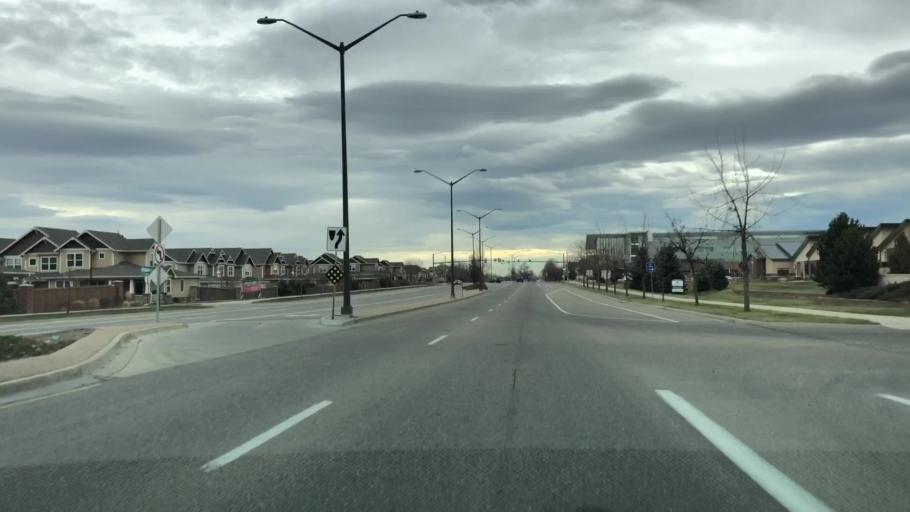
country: US
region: Colorado
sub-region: Larimer County
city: Fort Collins
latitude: 40.5603
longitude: -105.0393
